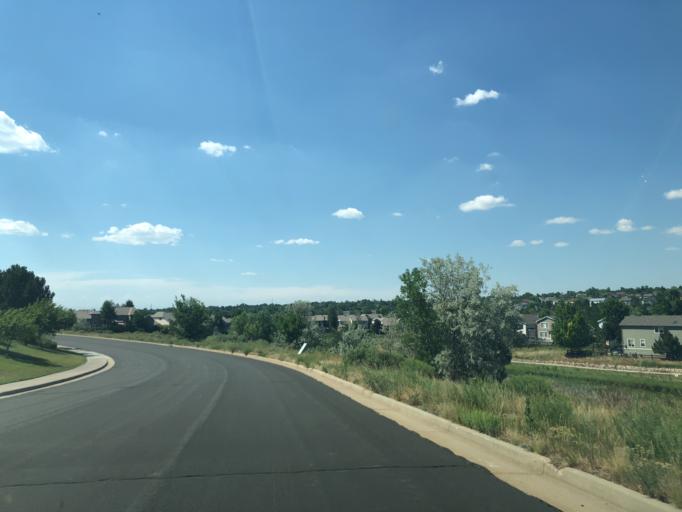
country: US
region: Colorado
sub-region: Arapahoe County
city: Dove Valley
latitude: 39.6055
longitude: -104.7794
